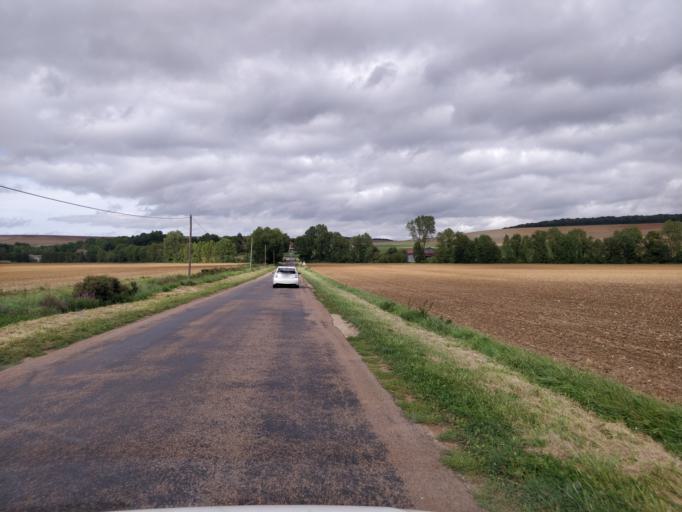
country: FR
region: Champagne-Ardenne
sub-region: Departement de l'Aube
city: Aix-en-Othe
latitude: 48.1983
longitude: 3.6355
